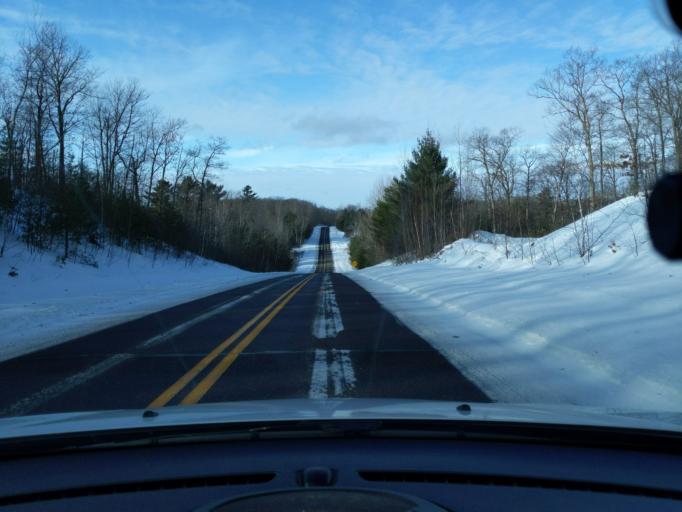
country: US
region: Wisconsin
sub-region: Sawyer County
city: Little Round Lake
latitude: 46.1153
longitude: -91.3313
